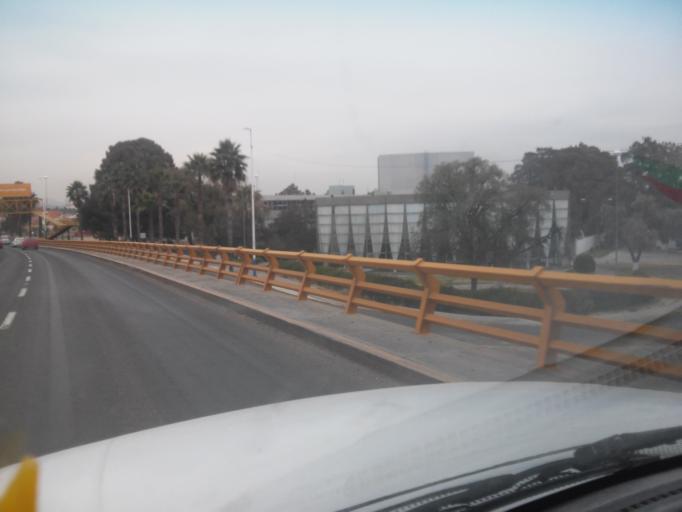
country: MX
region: Durango
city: Victoria de Durango
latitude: 24.0302
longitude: -104.6863
